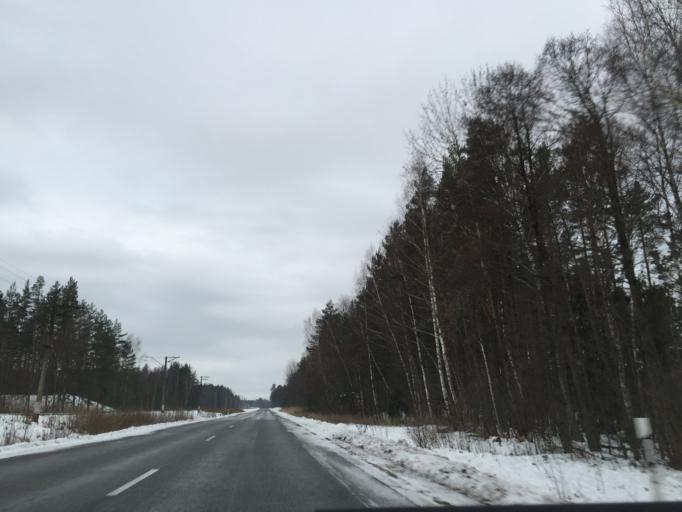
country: LV
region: Saulkrastu
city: Saulkrasti
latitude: 57.2066
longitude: 24.3782
